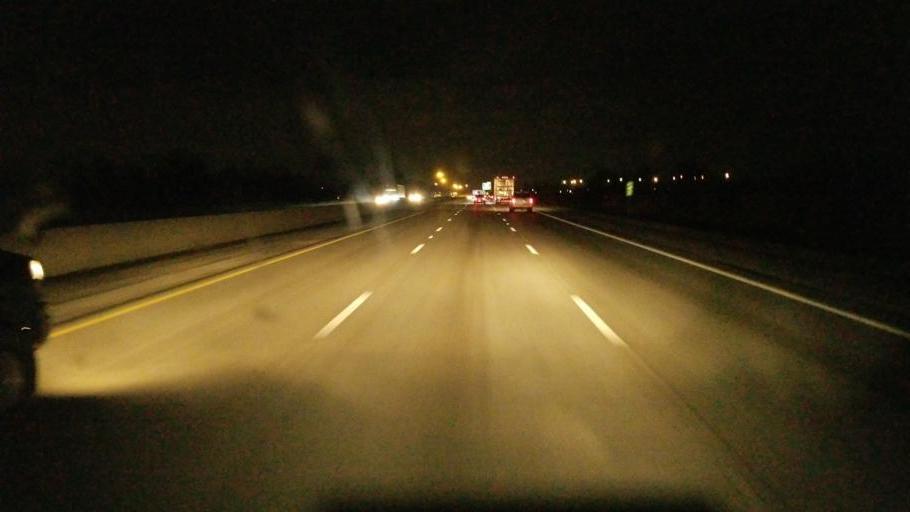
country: US
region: Ohio
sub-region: Clark County
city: Park Layne
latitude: 39.8650
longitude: -84.0359
